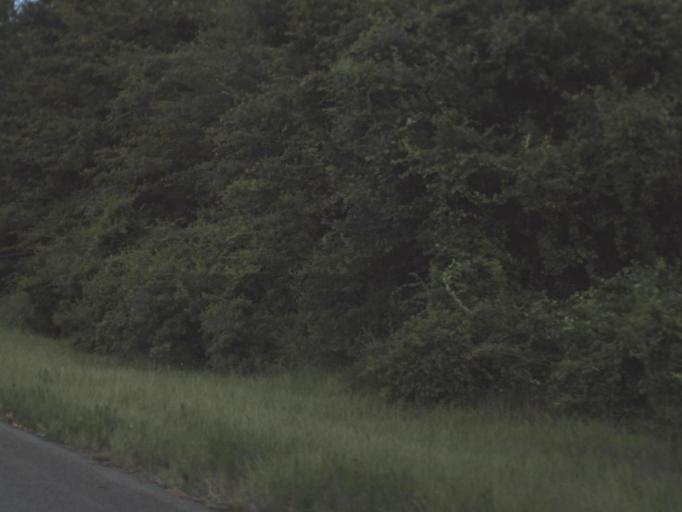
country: US
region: Florida
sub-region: Taylor County
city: Perry
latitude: 30.0909
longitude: -83.6440
